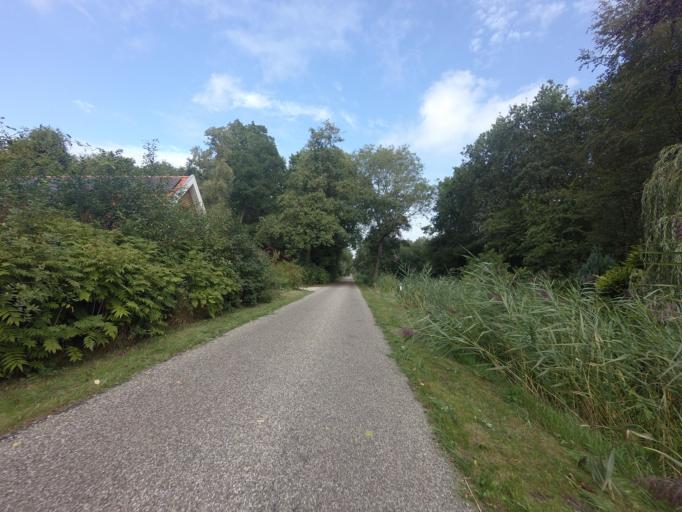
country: NL
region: Friesland
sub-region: Gemeente Heerenveen
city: Jubbega
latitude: 52.9890
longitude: 6.1124
